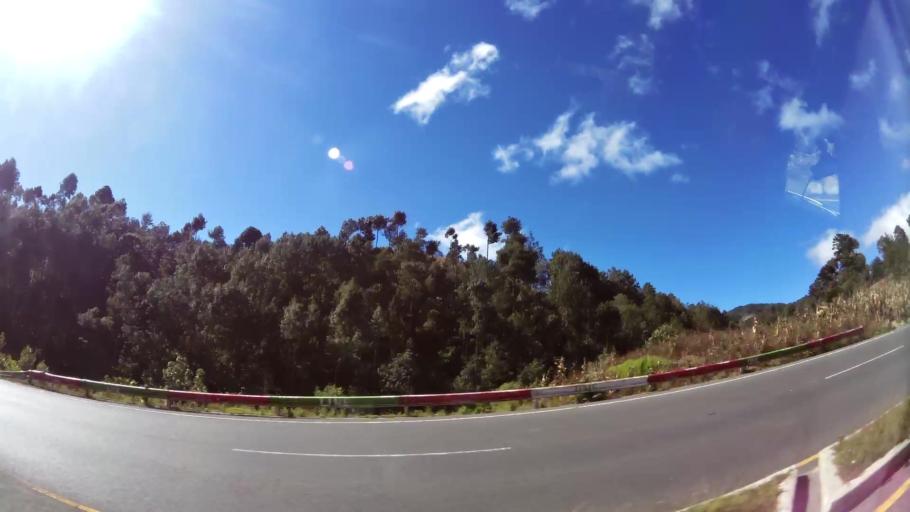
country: GT
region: Solola
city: Nahuala
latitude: 14.8327
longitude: -91.3302
